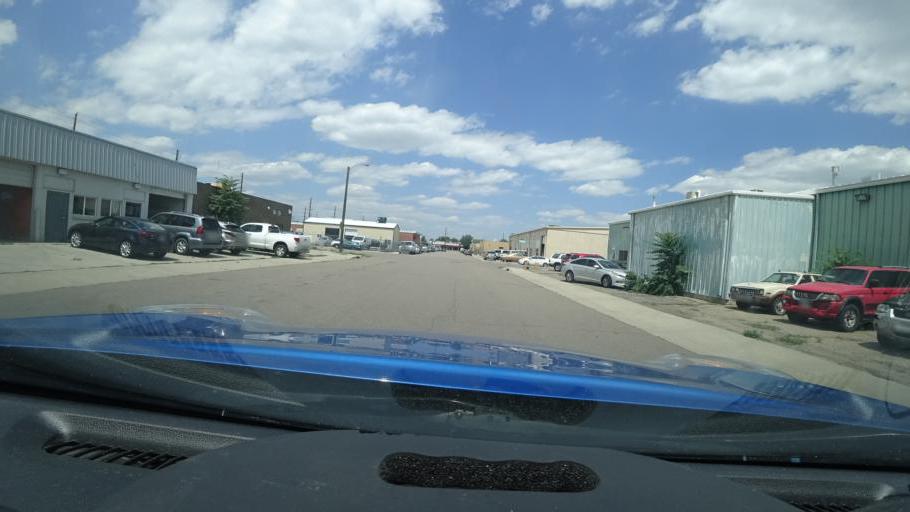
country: US
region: Colorado
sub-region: Arapahoe County
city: Englewood
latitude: 39.6762
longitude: -105.0006
